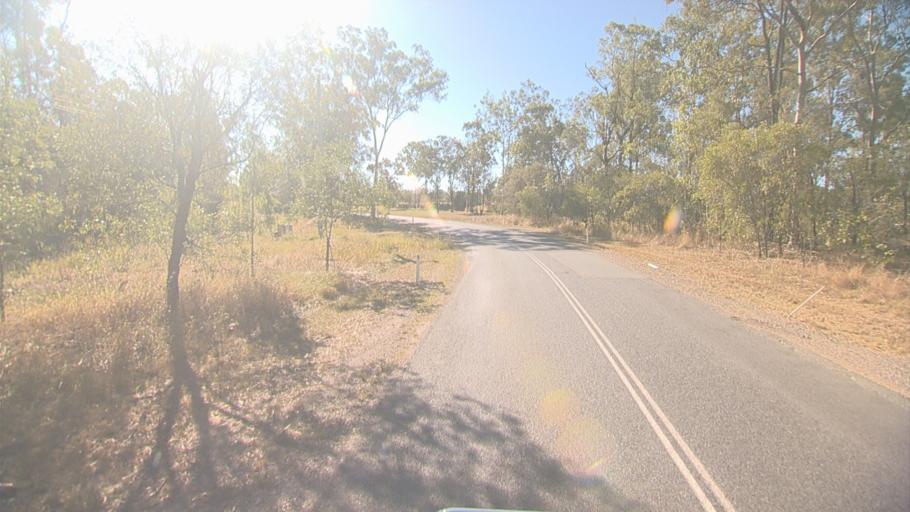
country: AU
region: Queensland
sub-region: Logan
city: North Maclean
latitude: -27.7547
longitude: 152.9960
